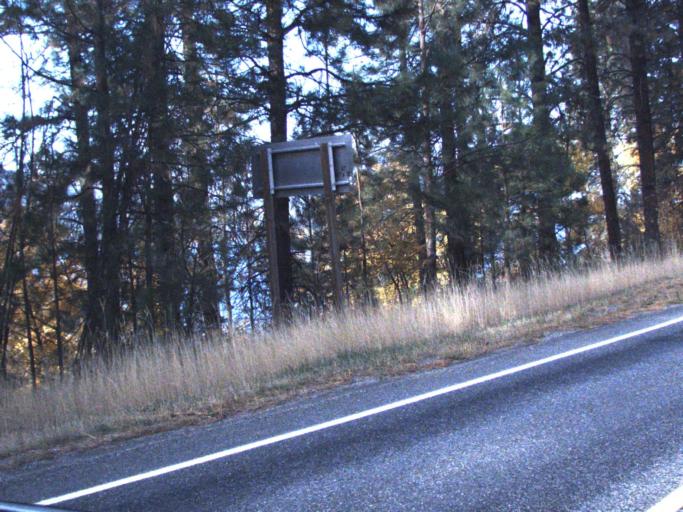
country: US
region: Washington
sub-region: Stevens County
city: Kettle Falls
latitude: 48.5179
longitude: -118.1423
